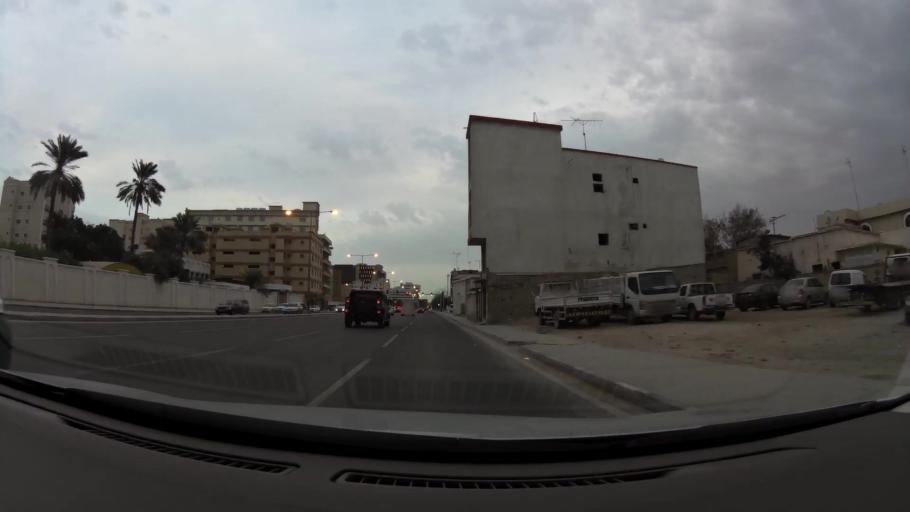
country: QA
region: Baladiyat ad Dawhah
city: Doha
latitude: 25.2705
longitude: 51.5267
